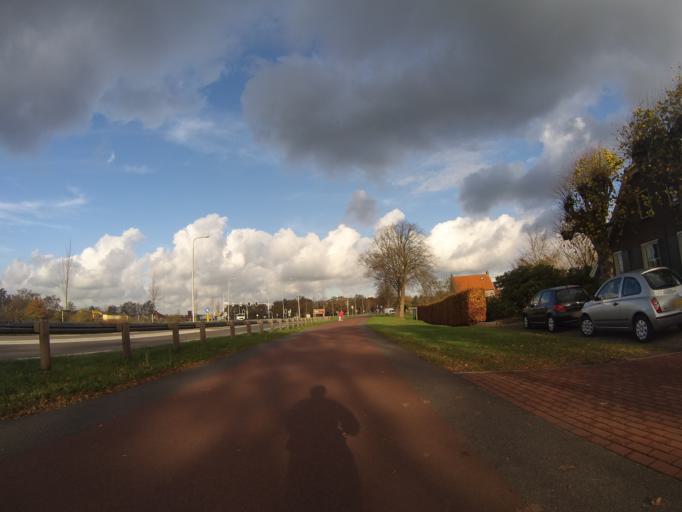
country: NL
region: Utrecht
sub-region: Gemeente Leusden
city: Leusden
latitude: 52.1775
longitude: 5.4363
